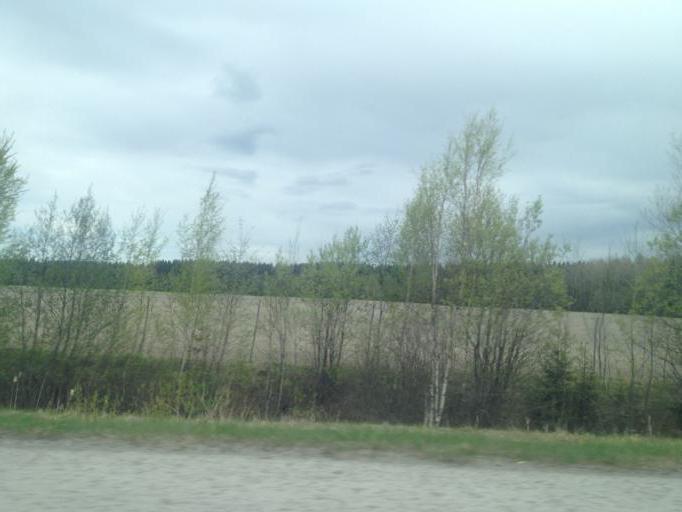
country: FI
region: Uusimaa
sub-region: Helsinki
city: Hyvinge
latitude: 60.5777
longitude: 24.8074
